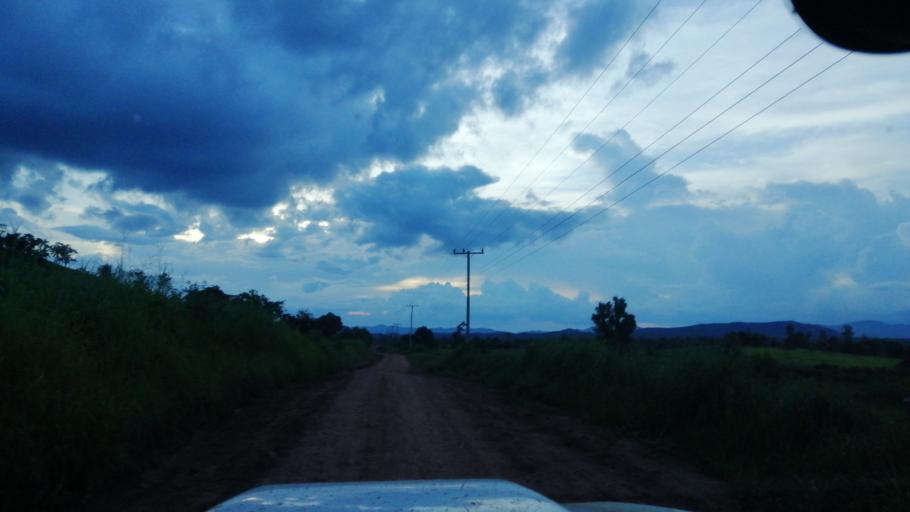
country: TH
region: Uttaradit
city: Ban Khok
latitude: 17.8775
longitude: 101.0692
